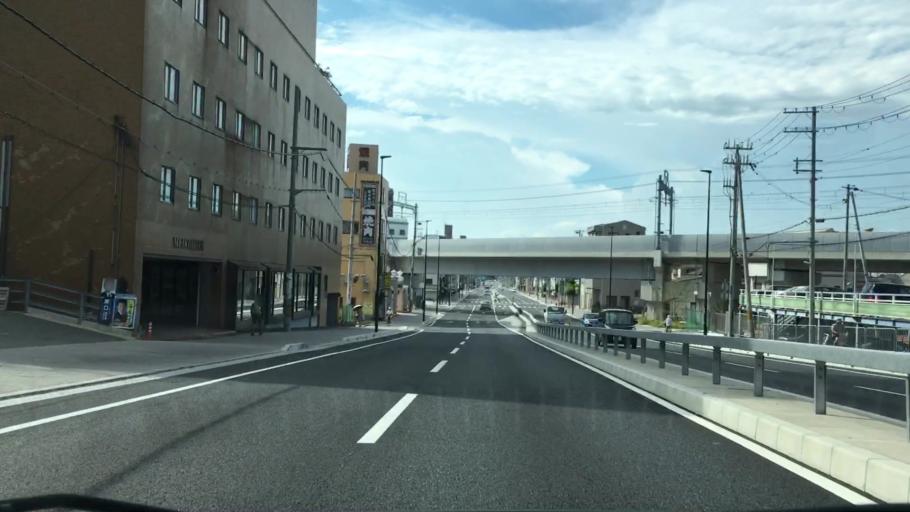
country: JP
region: Hyogo
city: Akashi
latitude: 34.6491
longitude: 134.9831
